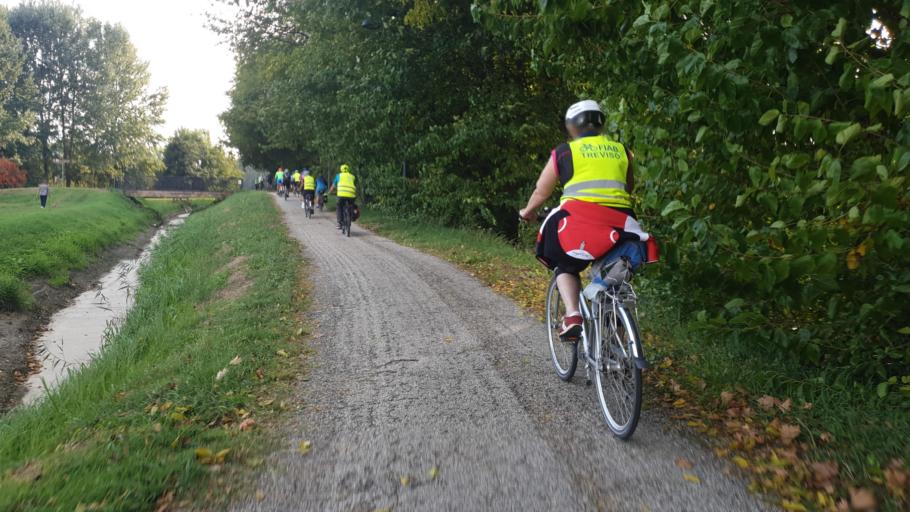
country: IT
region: Veneto
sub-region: Provincia di Padova
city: Montagnana
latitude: 45.2469
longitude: 11.4721
